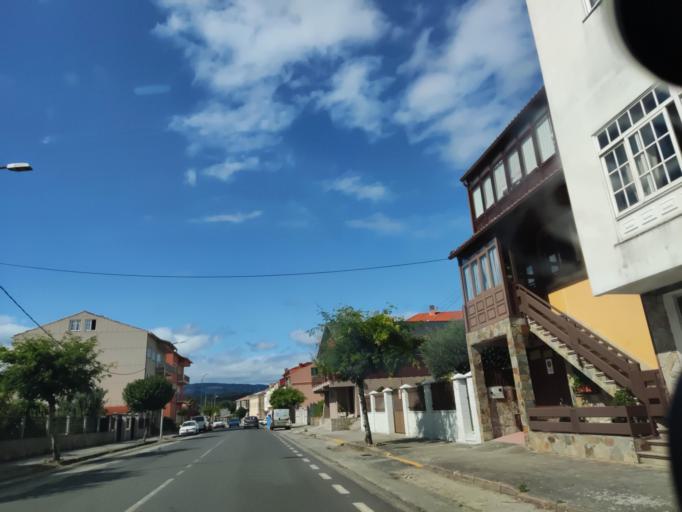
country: ES
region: Galicia
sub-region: Provincia da Coruna
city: Boiro
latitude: 42.6331
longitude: -8.8734
